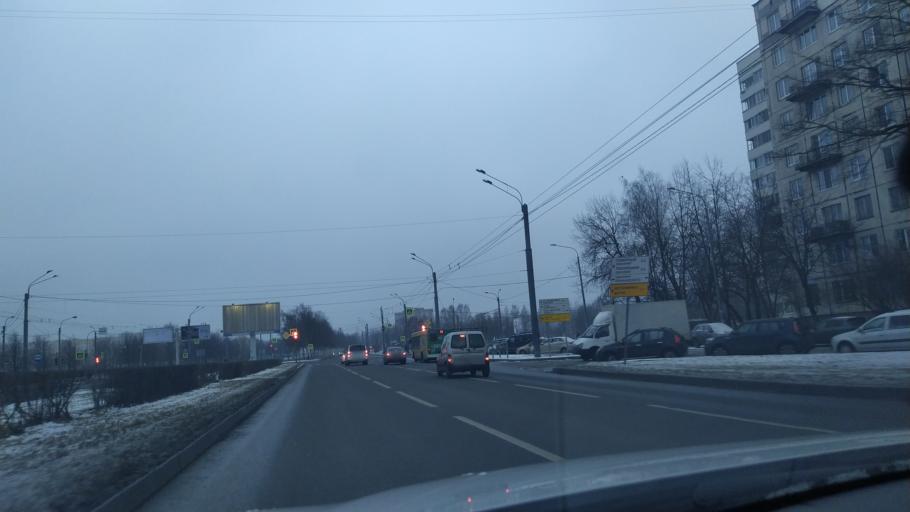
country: RU
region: St.-Petersburg
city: Grazhdanka
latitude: 60.0319
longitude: 30.3924
